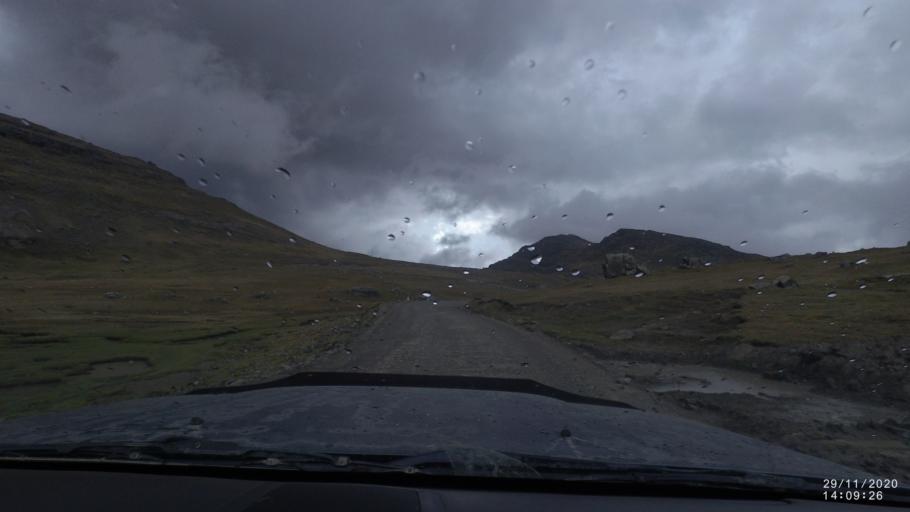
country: BO
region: Cochabamba
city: Sipe Sipe
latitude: -17.2272
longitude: -66.3859
